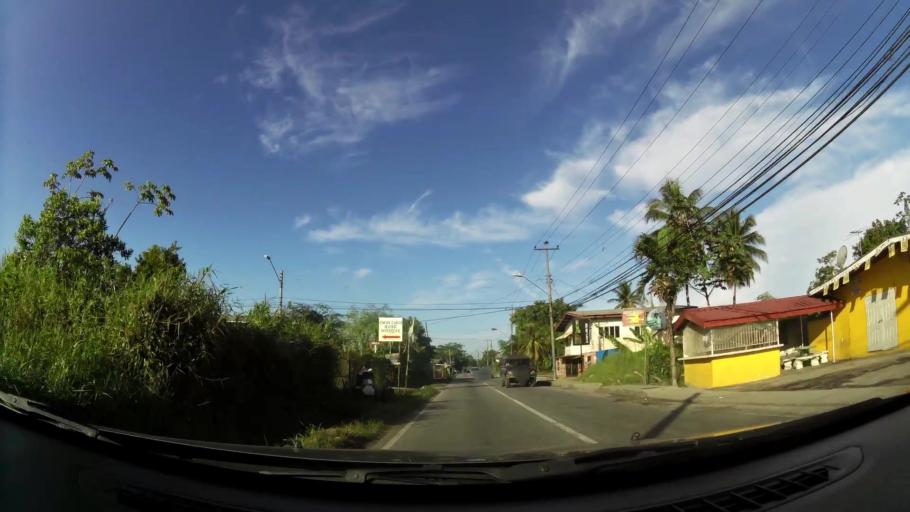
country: TT
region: Chaguanas
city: Chaguanas
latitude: 10.5470
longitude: -61.3518
